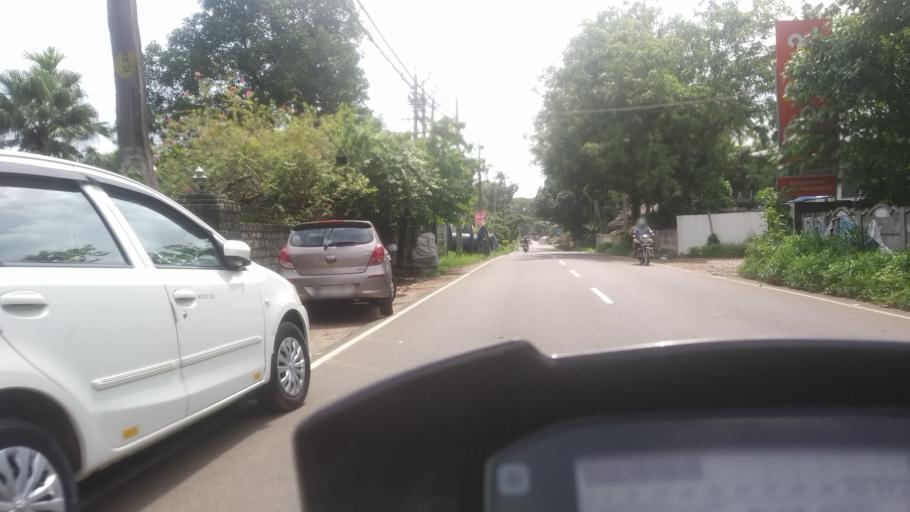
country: IN
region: Kerala
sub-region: Ernakulam
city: Elur
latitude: 10.1475
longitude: 76.2480
